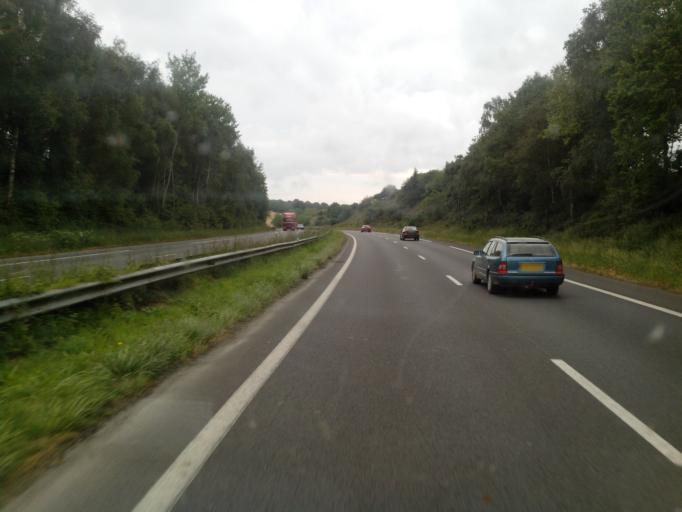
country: FR
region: Brittany
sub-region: Departement des Cotes-d'Armor
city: Lamballe
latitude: 48.4732
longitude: -2.5589
